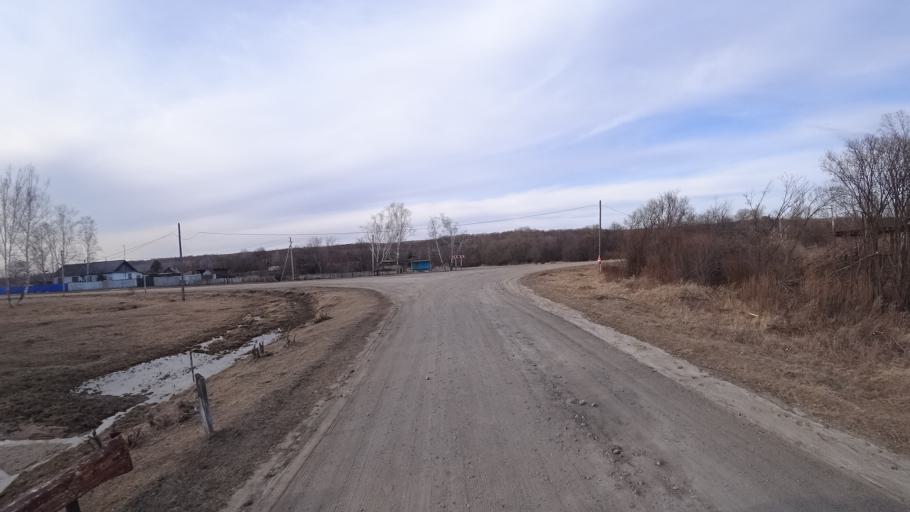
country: RU
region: Amur
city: Bureya
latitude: 50.0196
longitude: 129.7733
